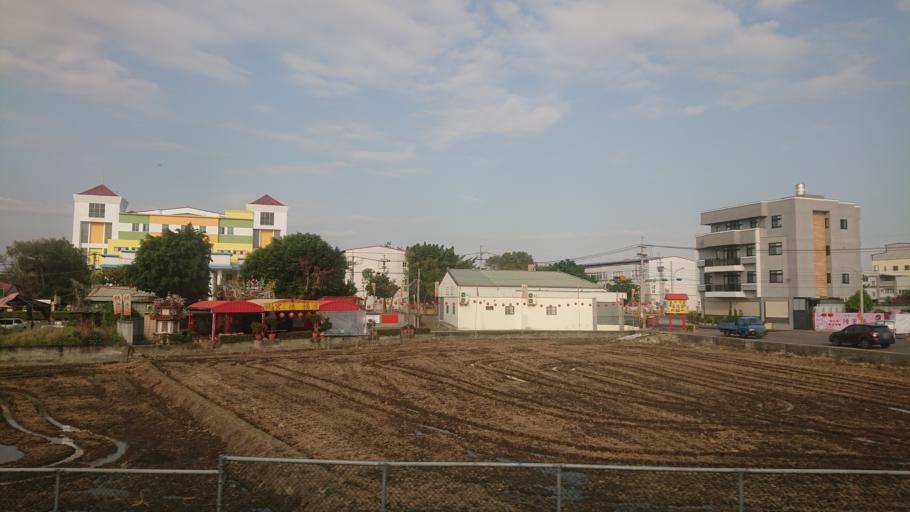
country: TW
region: Taiwan
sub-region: Yunlin
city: Douliu
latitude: 23.6670
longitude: 120.4761
